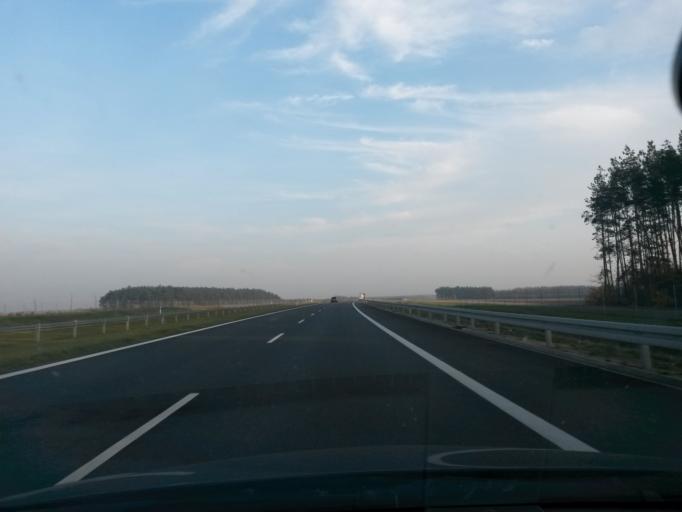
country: PL
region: Lodz Voivodeship
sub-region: Powiat wieruszowski
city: Wieruszow
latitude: 51.3369
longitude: 18.1296
